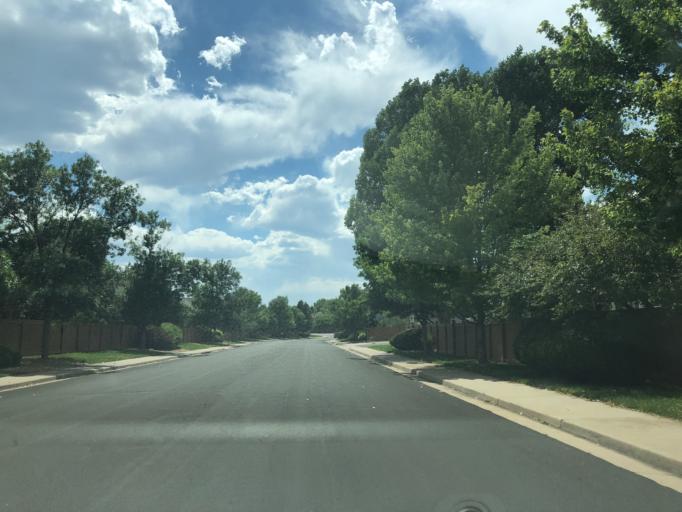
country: US
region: Colorado
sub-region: Arapahoe County
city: Dove Valley
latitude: 39.6220
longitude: -104.7701
